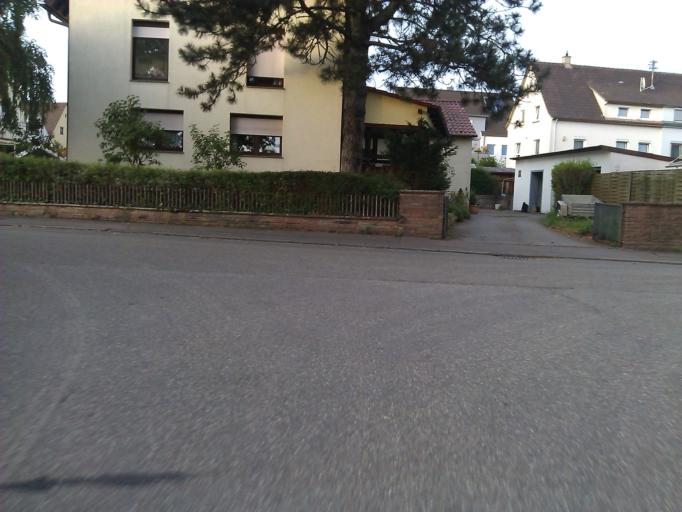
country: DE
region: Baden-Wuerttemberg
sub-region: Regierungsbezirk Stuttgart
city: Brackenheim
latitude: 49.0765
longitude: 9.0717
